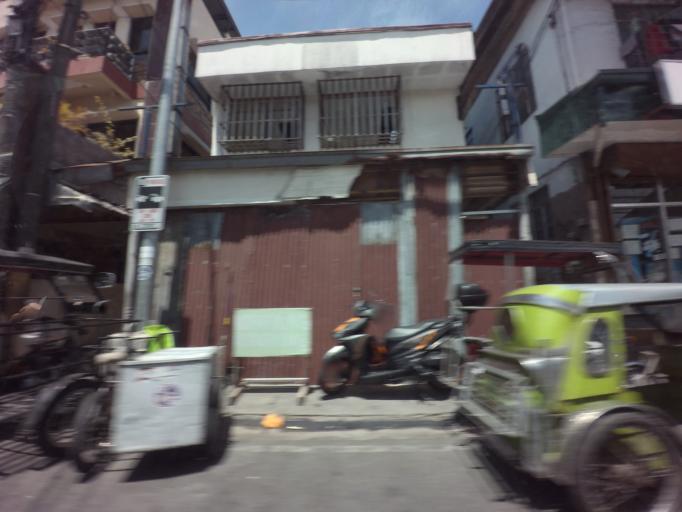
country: PH
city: Sambayanihan People's Village
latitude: 14.5055
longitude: 120.9940
